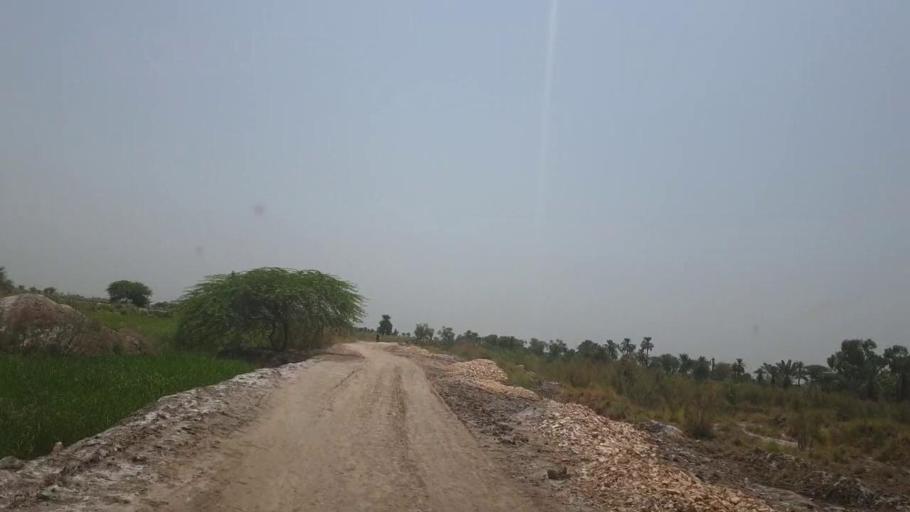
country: PK
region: Sindh
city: Lakhi
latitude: 27.8620
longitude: 68.6635
